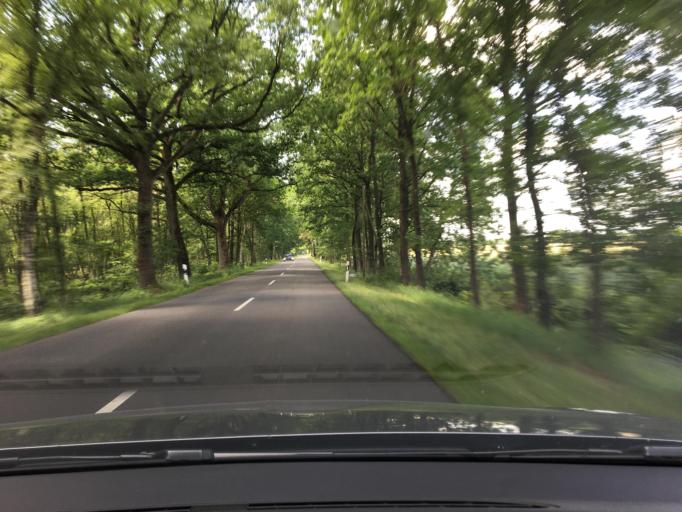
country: DE
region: Lower Saxony
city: Kirchtimke
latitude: 53.2496
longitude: 9.2011
